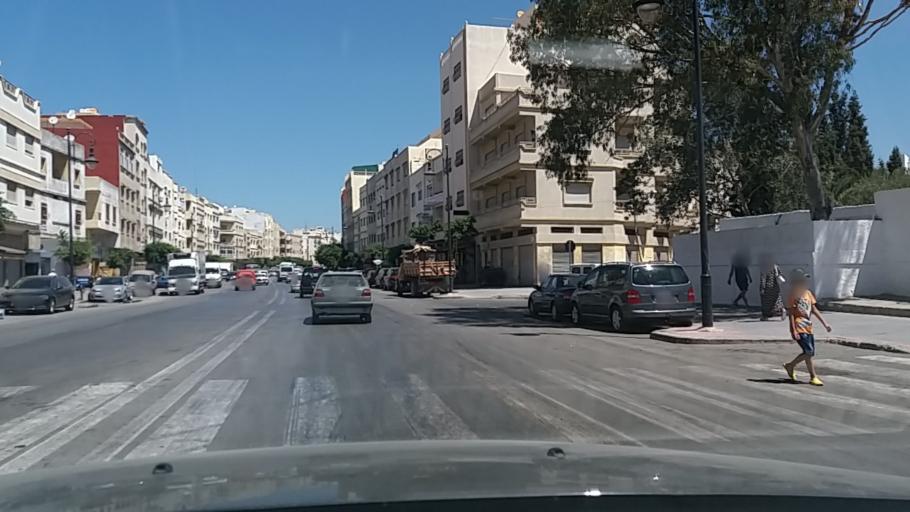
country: MA
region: Tanger-Tetouan
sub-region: Tanger-Assilah
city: Tangier
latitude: 35.7589
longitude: -5.7961
